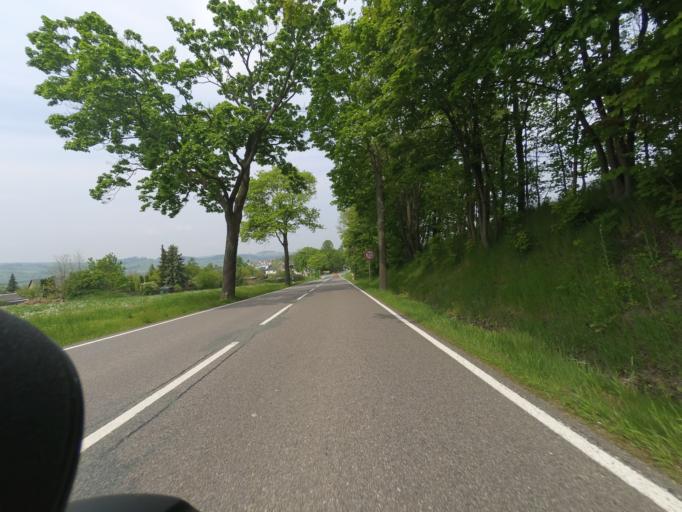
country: DE
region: Saxony
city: Wolkenstein
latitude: 50.6516
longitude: 13.0820
